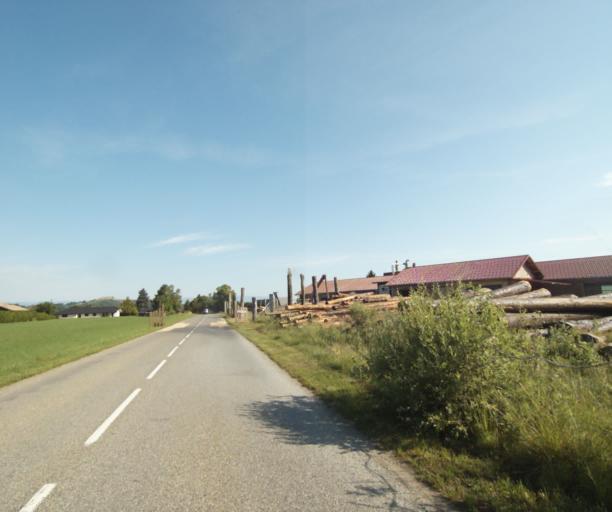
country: FR
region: Rhone-Alpes
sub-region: Departement de la Haute-Savoie
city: Allinges
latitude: 46.3133
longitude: 6.4857
